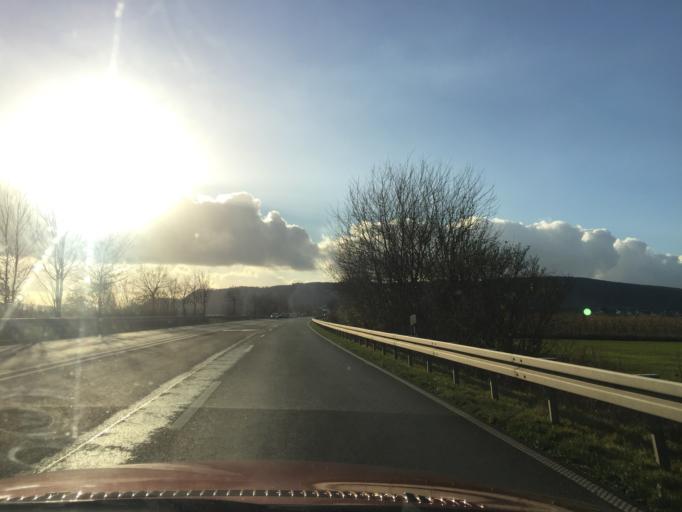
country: DE
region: Lower Saxony
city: Holzminden
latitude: 51.8248
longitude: 9.4258
